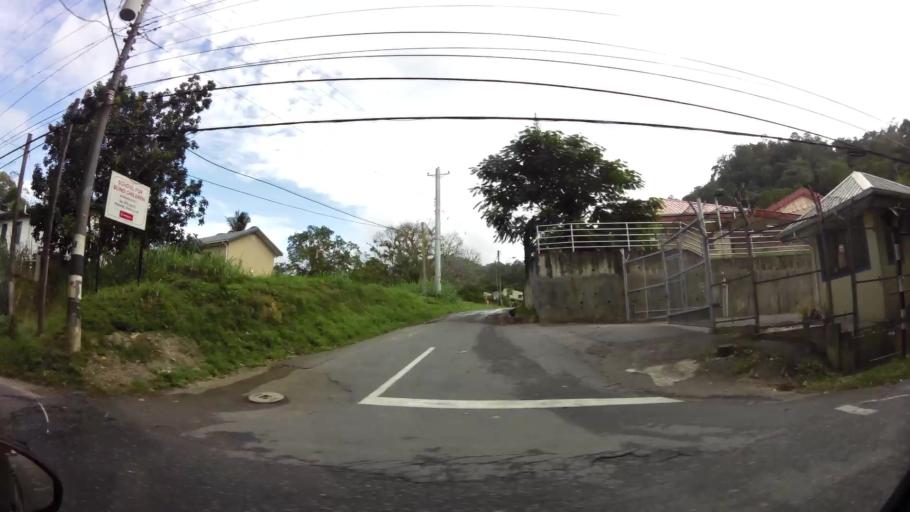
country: TT
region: San Juan/Laventille
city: Laventille
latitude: 10.7050
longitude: -61.4604
